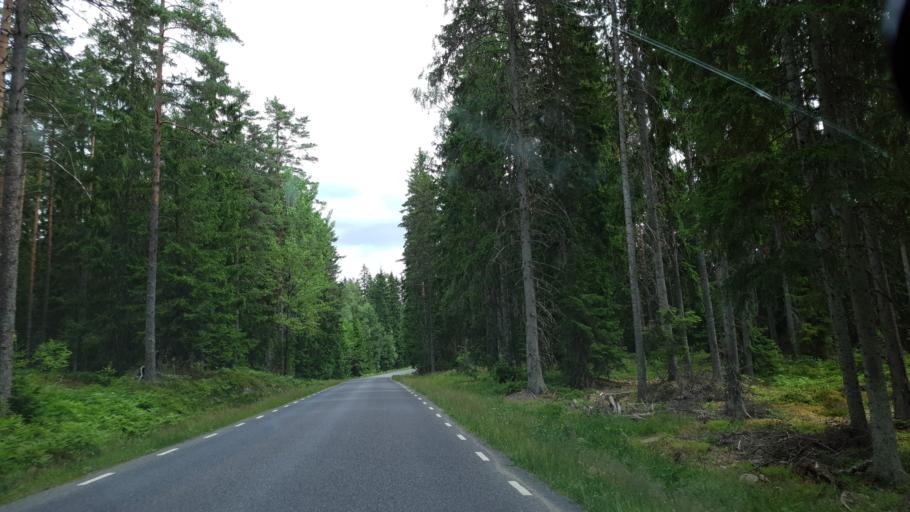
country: SE
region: Kronoberg
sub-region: Uppvidinge Kommun
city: Aseda
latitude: 57.1911
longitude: 15.3954
